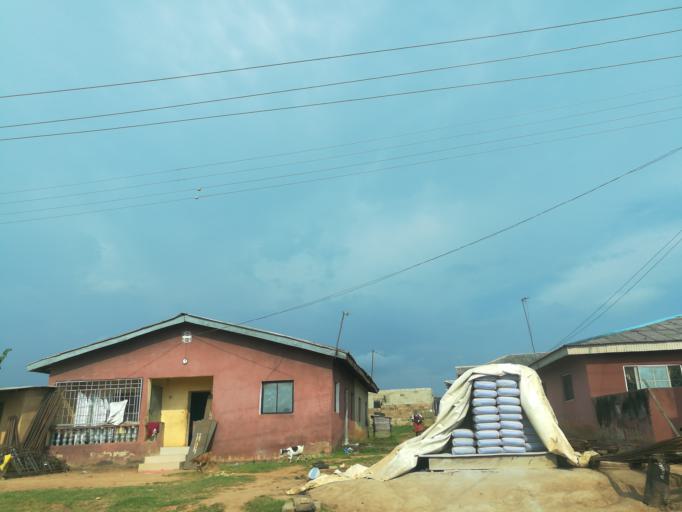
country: NG
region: Lagos
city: Ikorodu
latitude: 6.6664
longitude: 3.6661
